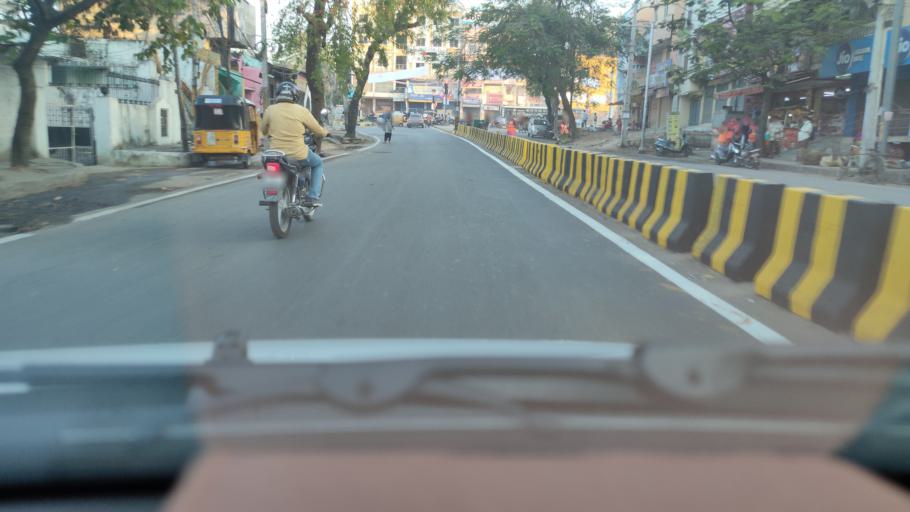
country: IN
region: Telangana
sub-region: Rangareddi
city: Gaddi Annaram
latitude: 17.3912
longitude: 78.5163
